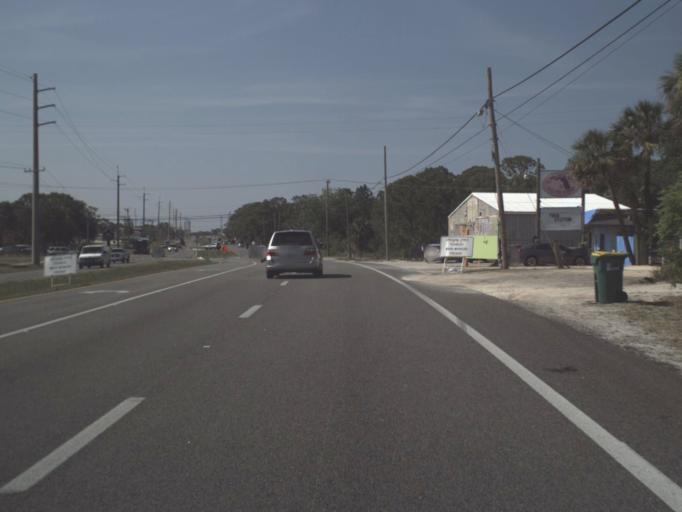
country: US
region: Florida
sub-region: Brevard County
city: Sharpes
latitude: 28.4591
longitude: -80.7629
